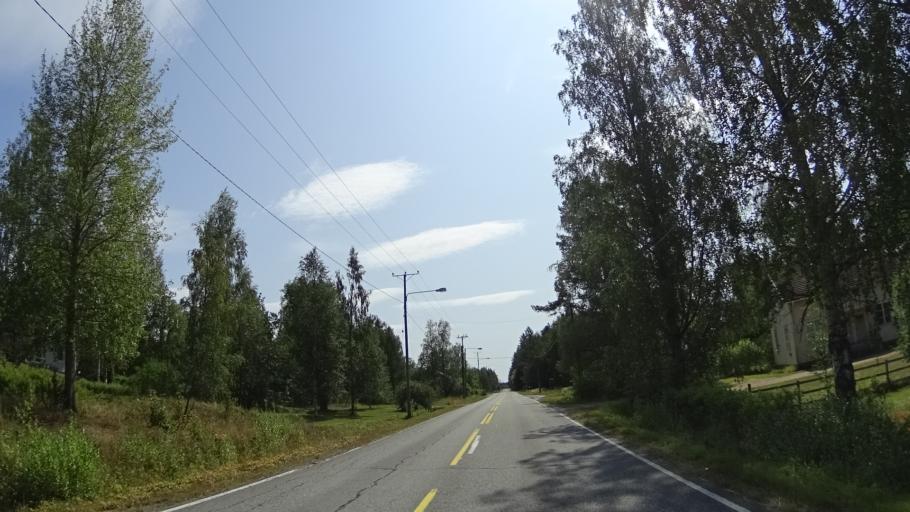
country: FI
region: Pirkanmaa
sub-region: Ylae-Pirkanmaa
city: Maenttae
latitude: 61.9069
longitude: 24.7866
